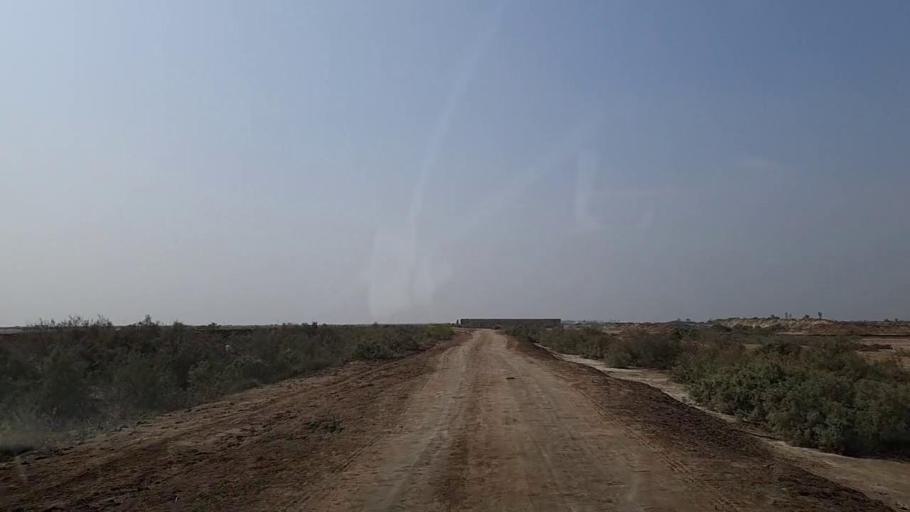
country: PK
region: Sindh
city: Gharo
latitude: 24.6737
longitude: 67.7138
